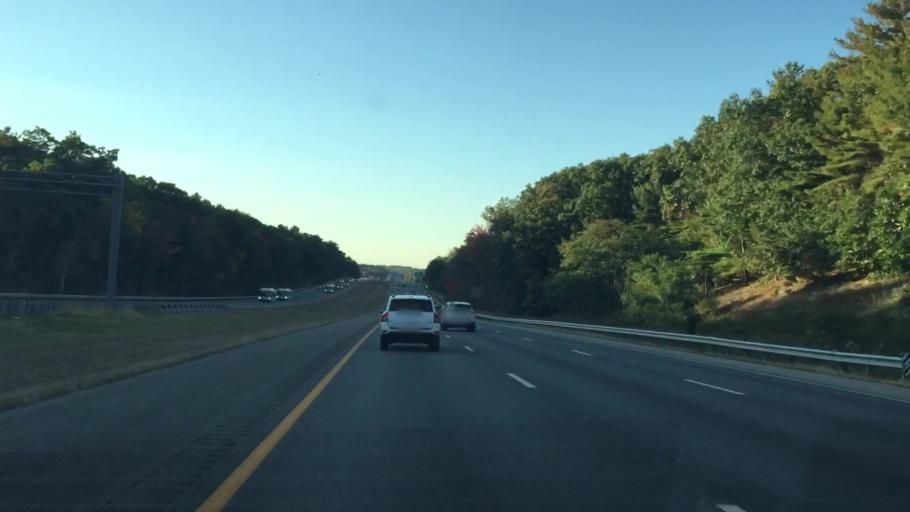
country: US
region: Massachusetts
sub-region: Middlesex County
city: Pinehurst
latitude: 42.4938
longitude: -71.2347
